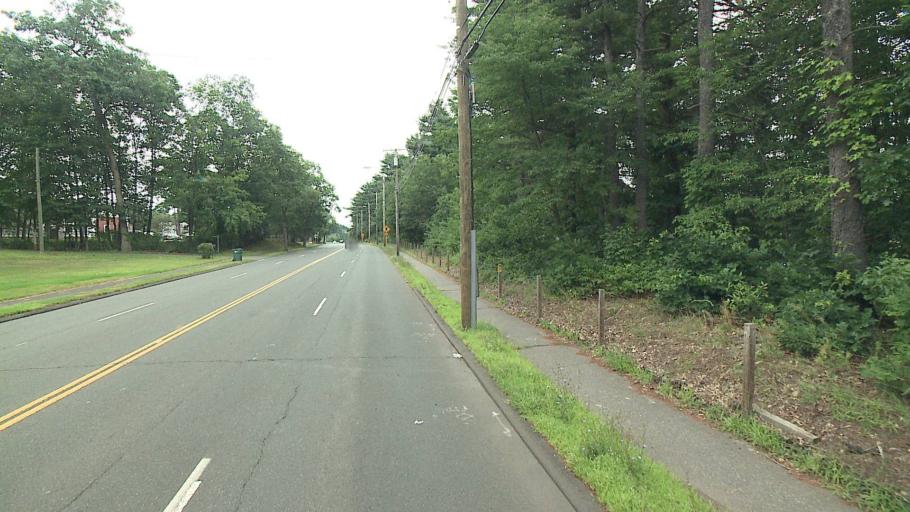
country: US
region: Connecticut
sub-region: New Haven County
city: New Haven
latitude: 41.3506
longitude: -72.9132
